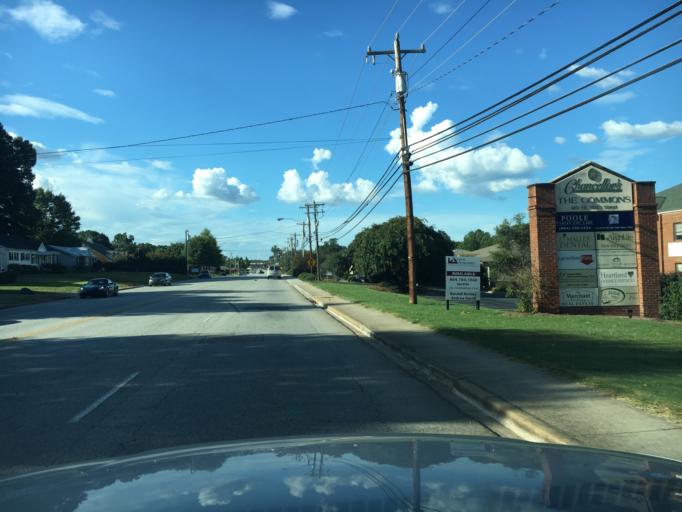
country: US
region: South Carolina
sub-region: Greenville County
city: Simpsonville
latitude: 34.7288
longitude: -82.2541
